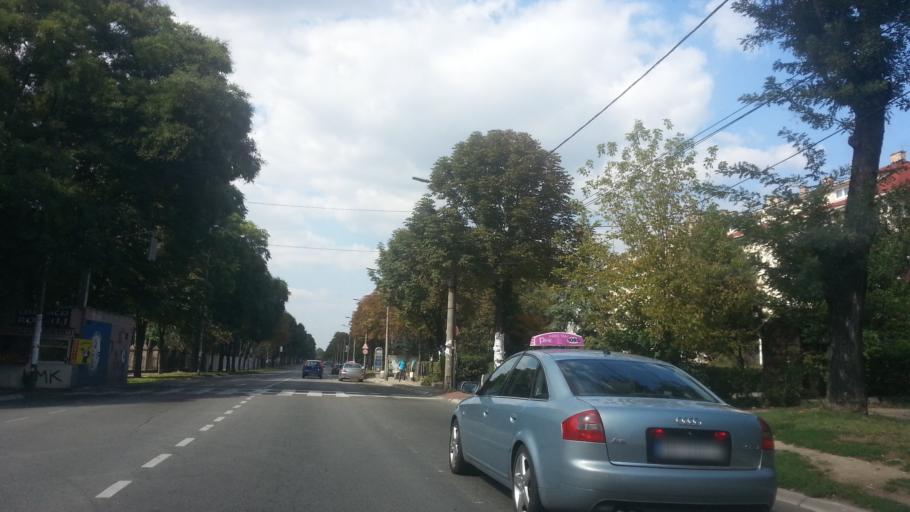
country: RS
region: Central Serbia
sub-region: Belgrade
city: Zemun
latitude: 44.8549
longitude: 20.3874
